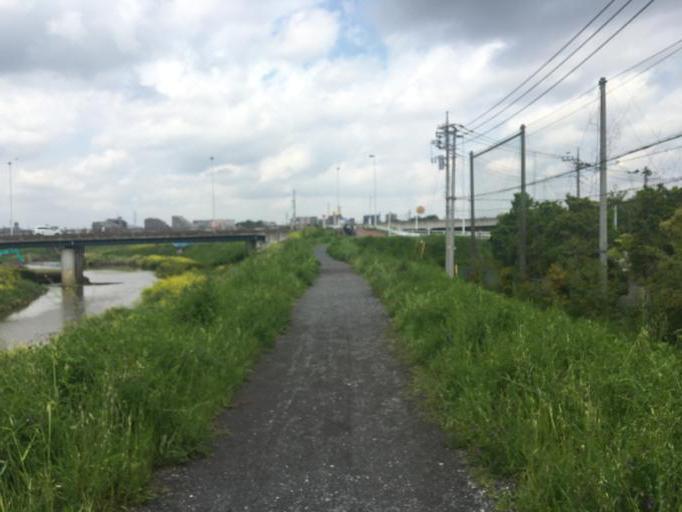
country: JP
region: Saitama
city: Kawagoe
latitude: 35.8998
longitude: 139.4981
